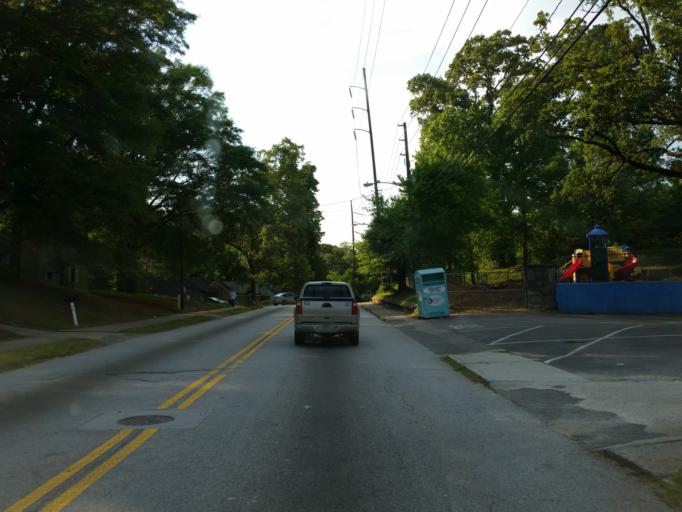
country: US
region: Georgia
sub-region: Fulton County
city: Atlanta
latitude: 33.7698
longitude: -84.4725
